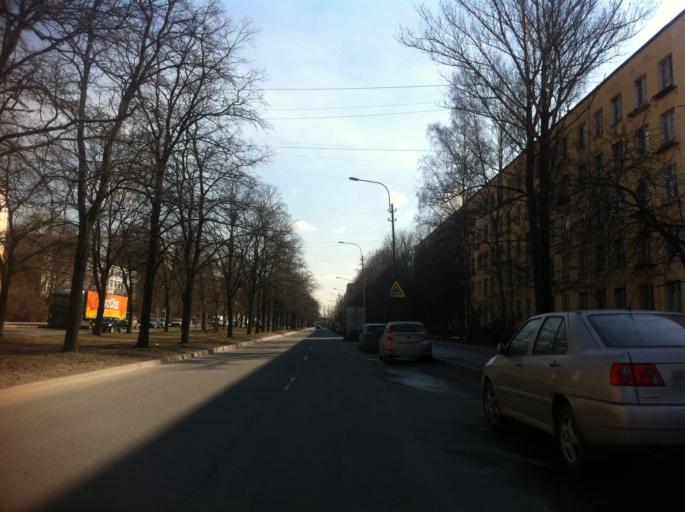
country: RU
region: St.-Petersburg
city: Dachnoye
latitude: 59.8428
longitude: 30.2667
